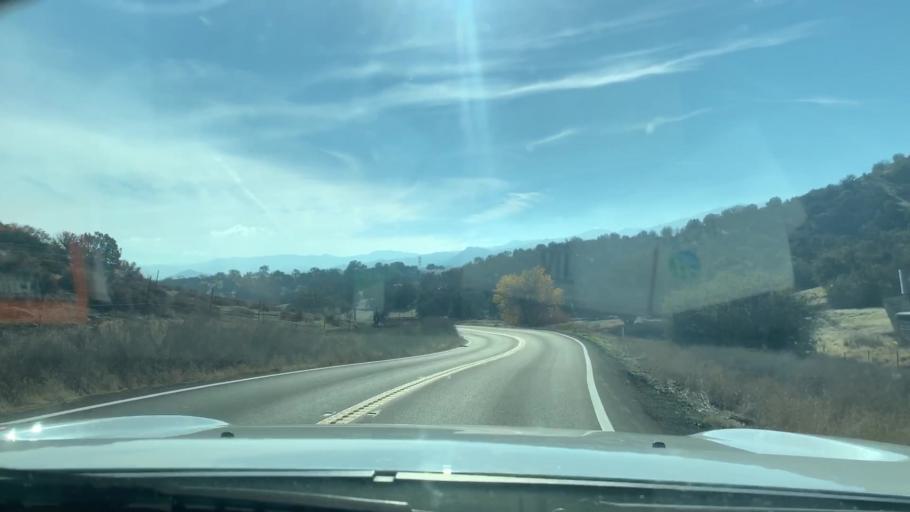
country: US
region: California
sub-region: Fresno County
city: Coalinga
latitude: 36.0845
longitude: -120.4881
